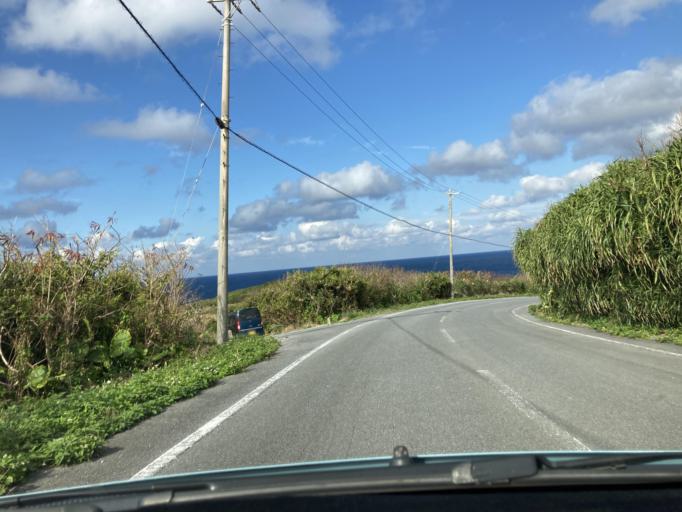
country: JP
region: Okinawa
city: Nago
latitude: 26.8699
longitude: 128.2611
